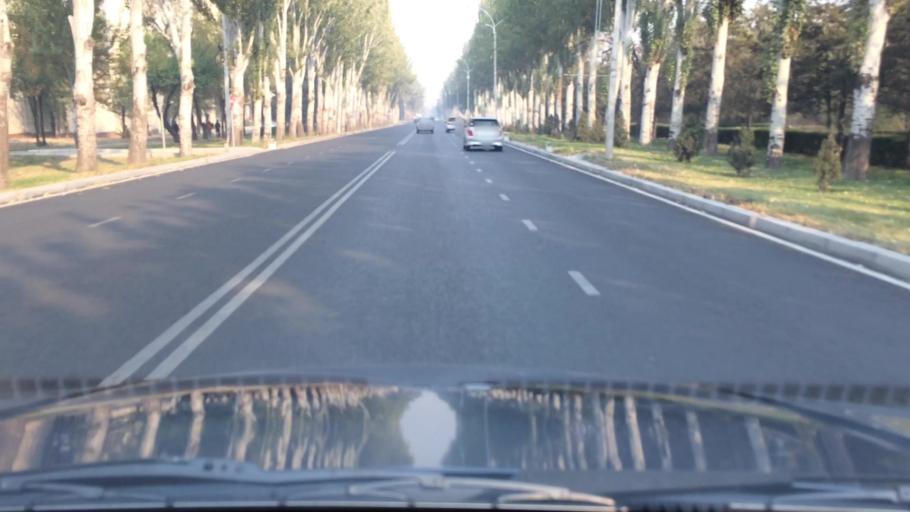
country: KG
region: Chuy
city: Bishkek
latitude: 42.8346
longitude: 74.5856
